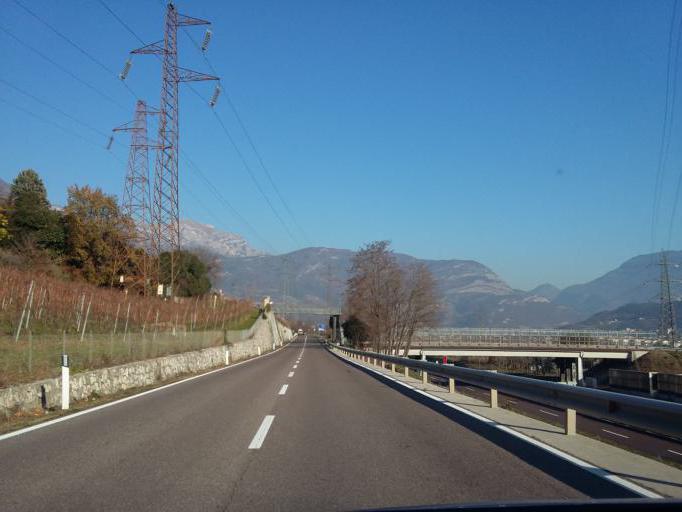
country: IT
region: Trentino-Alto Adige
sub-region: Provincia di Trento
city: Isera
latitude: 45.8837
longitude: 11.0104
